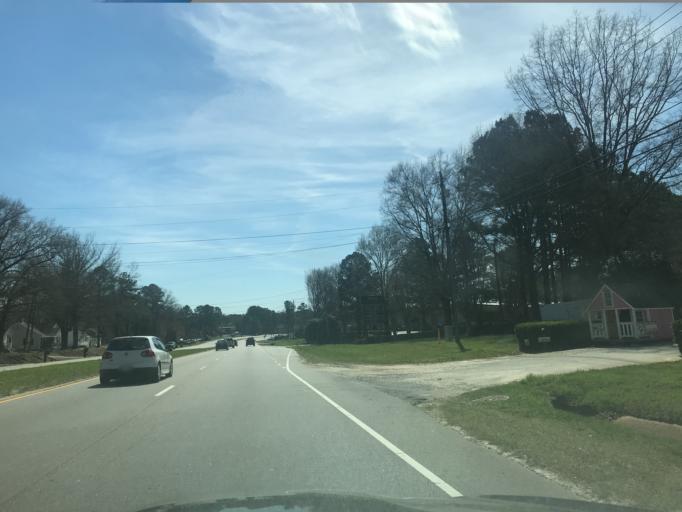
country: US
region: North Carolina
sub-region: Wake County
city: Garner
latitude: 35.7097
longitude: -78.6591
